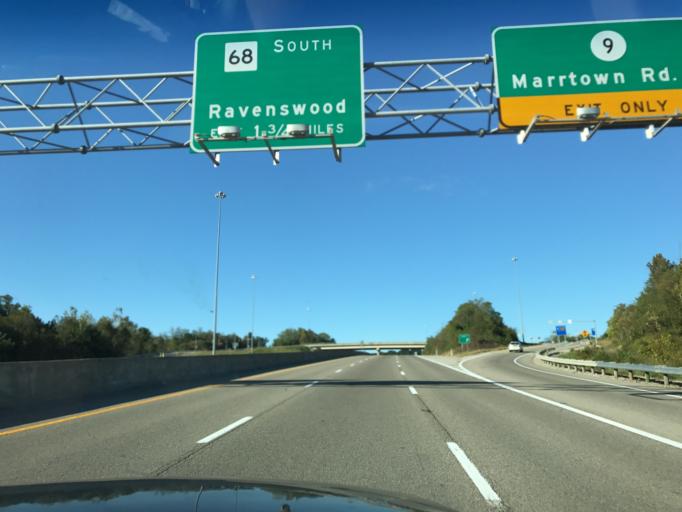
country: US
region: Ohio
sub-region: Washington County
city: Belpre
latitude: 39.2594
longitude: -81.5777
